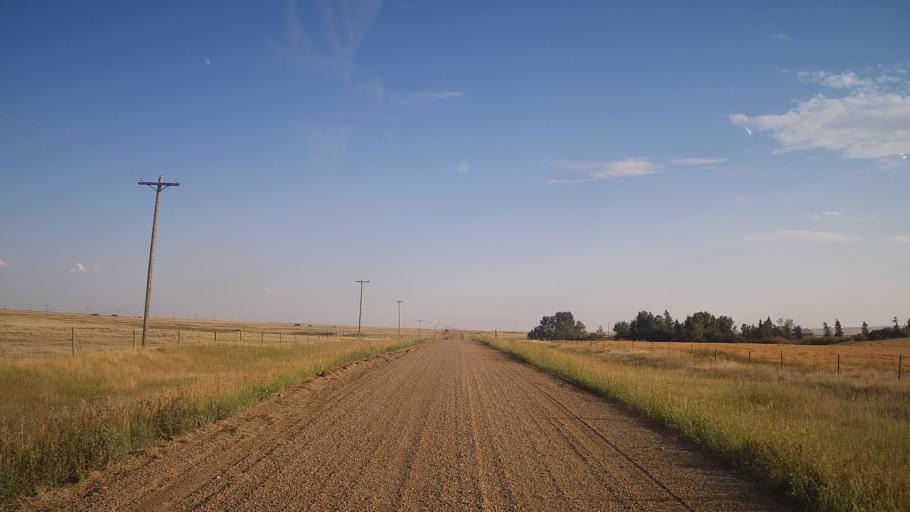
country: CA
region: Alberta
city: Hanna
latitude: 51.6150
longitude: -111.8569
